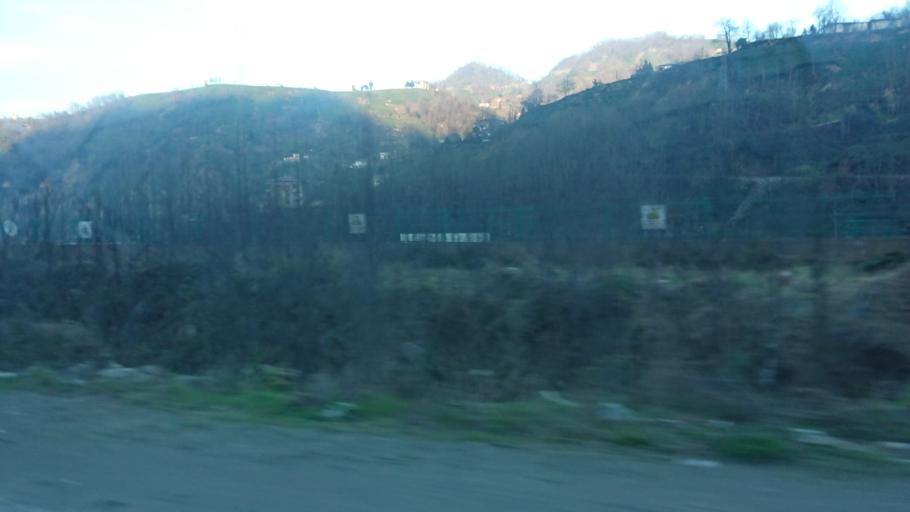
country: TR
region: Rize
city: Gundogdu
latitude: 41.0227
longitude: 40.5766
